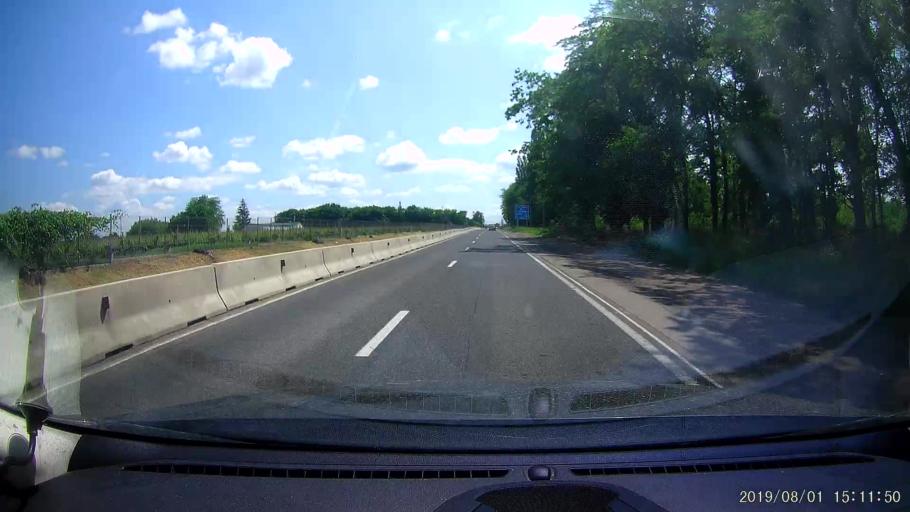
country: RO
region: Braila
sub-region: Comuna Chiscani
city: Chiscani
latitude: 45.2135
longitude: 27.9203
